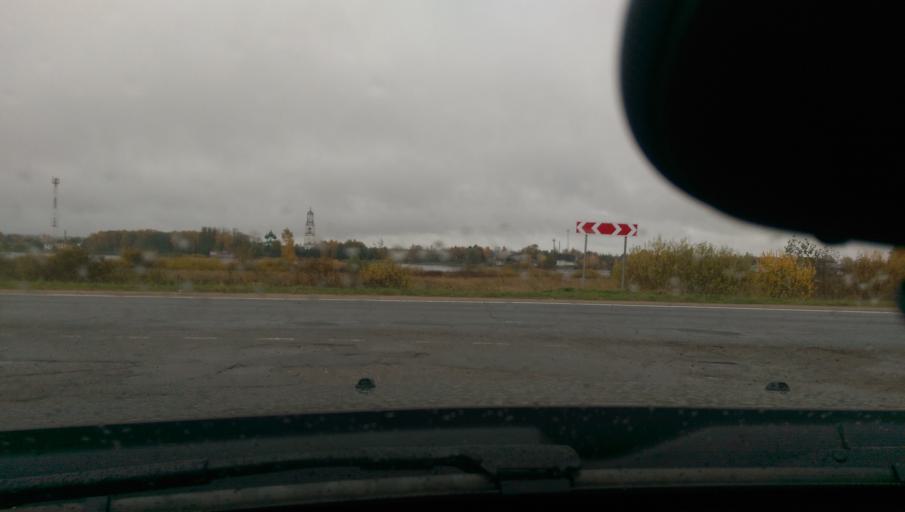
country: RU
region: Jaroslavl
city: Poshekhon'ye
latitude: 58.5107
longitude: 39.1148
